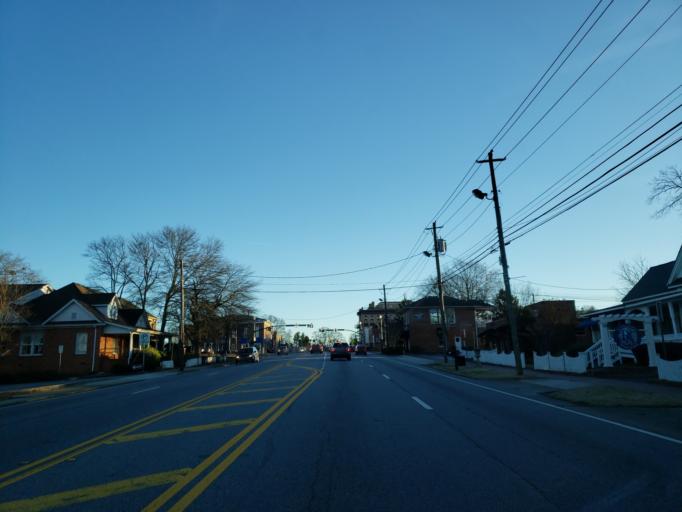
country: US
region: Georgia
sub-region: Fulton County
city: Alpharetta
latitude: 34.0769
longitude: -84.2945
